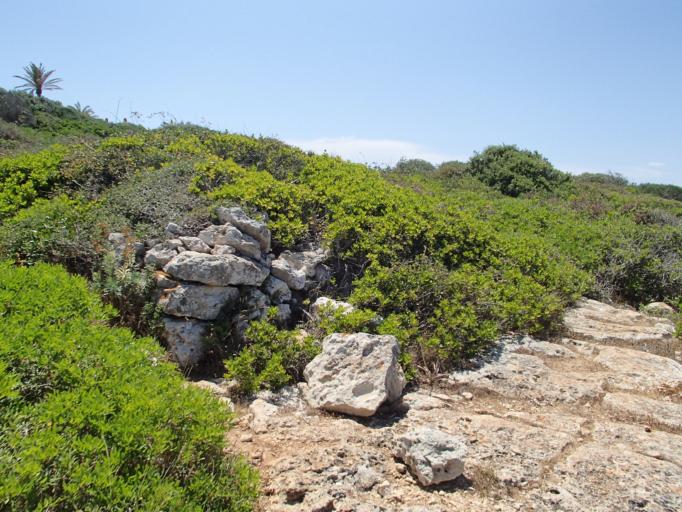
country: ES
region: Balearic Islands
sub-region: Illes Balears
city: Es Castell
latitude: 39.8403
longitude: 4.2989
